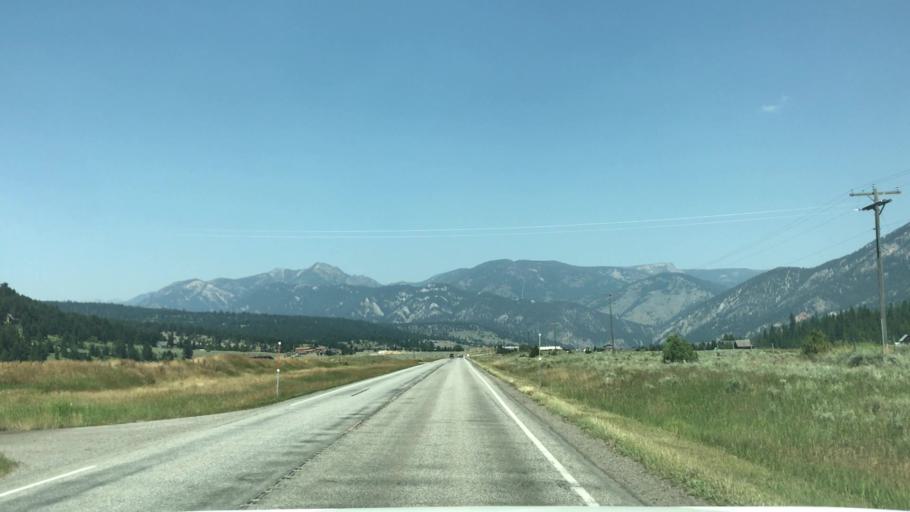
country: US
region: Montana
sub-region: Gallatin County
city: Big Sky
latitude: 45.2136
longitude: -111.2480
